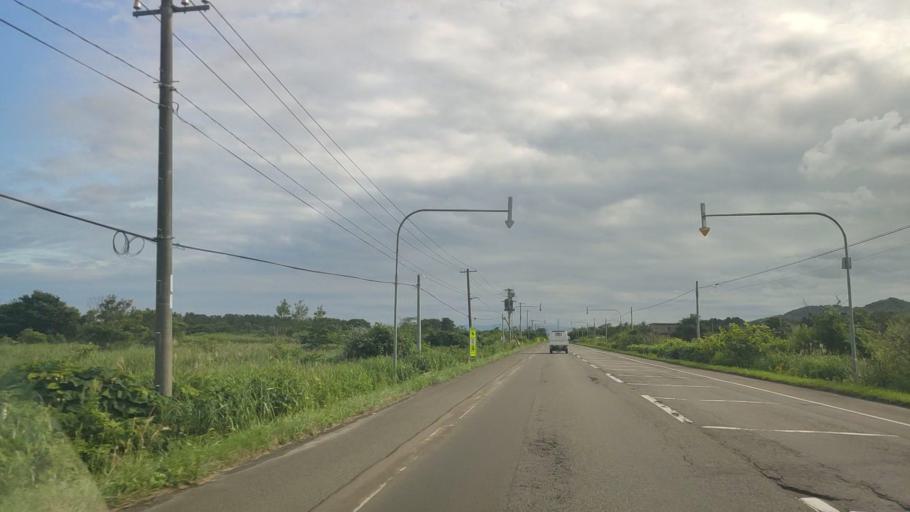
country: JP
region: Hokkaido
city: Niseko Town
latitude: 42.4668
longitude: 140.3404
